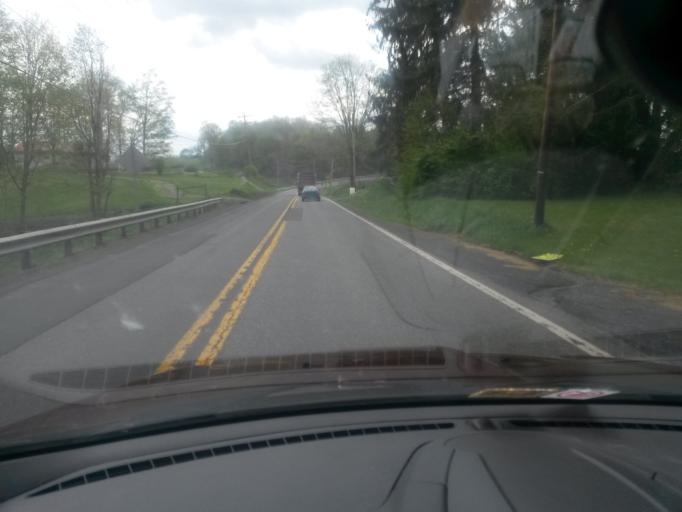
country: US
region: West Virginia
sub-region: Greenbrier County
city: Lewisburg
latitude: 37.8781
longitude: -80.4118
